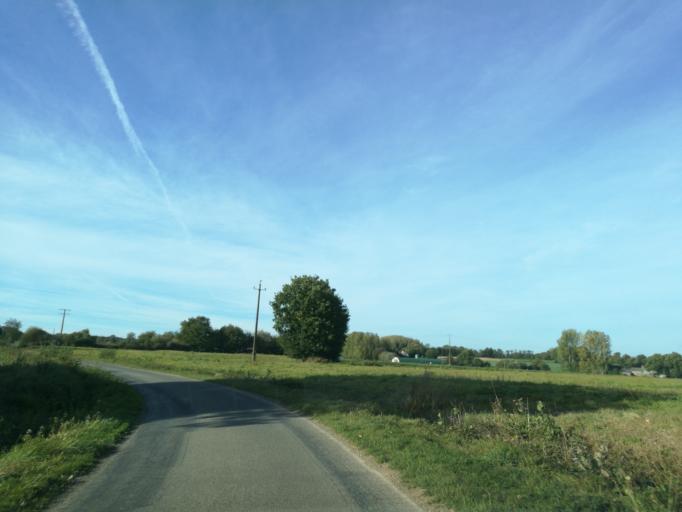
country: FR
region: Brittany
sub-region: Departement d'Ille-et-Vilaine
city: Bedee
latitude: 48.2038
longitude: -1.9544
